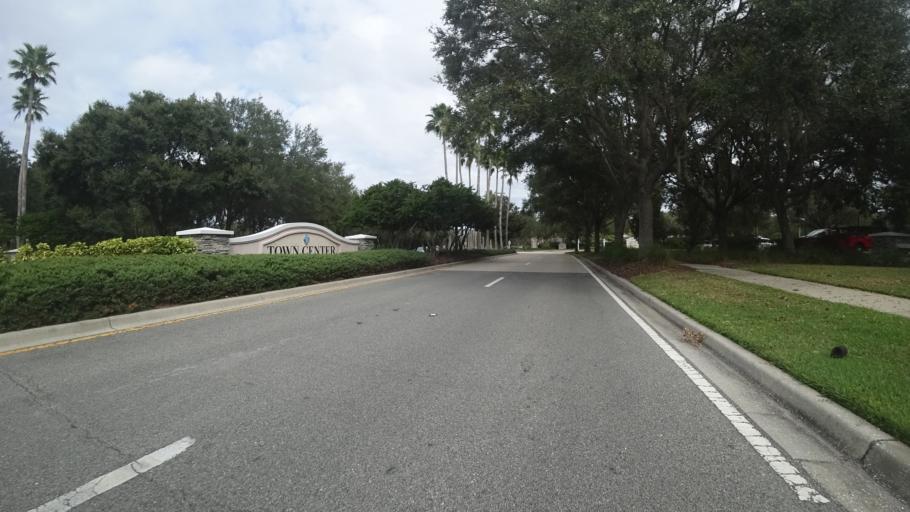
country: US
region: Florida
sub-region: Sarasota County
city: The Meadows
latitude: 27.3871
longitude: -82.4374
